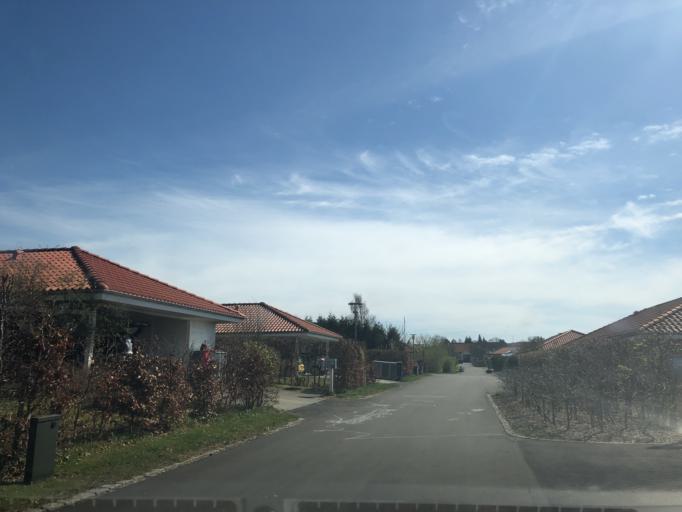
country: DK
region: Zealand
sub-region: Ringsted Kommune
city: Ringsted
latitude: 55.4550
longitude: 11.7722
